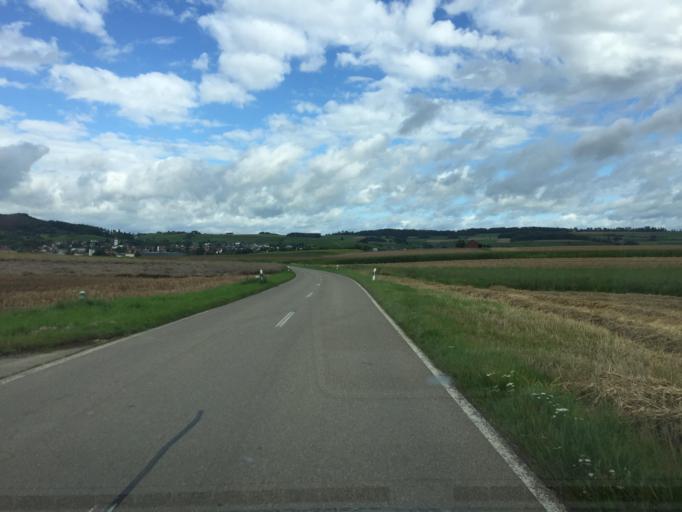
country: CH
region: Schaffhausen
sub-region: Bezirk Unterklettgau
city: Wilchingen
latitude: 47.6547
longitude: 8.4435
